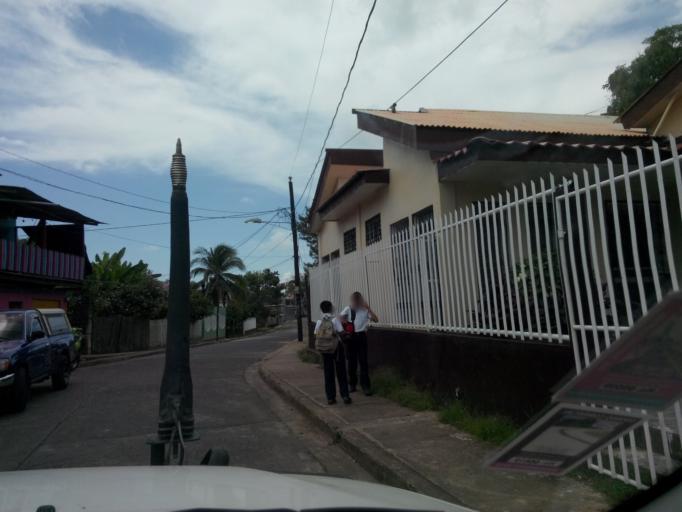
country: NI
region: Atlantico Sur
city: Bluefields
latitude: 12.0092
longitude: -83.7607
